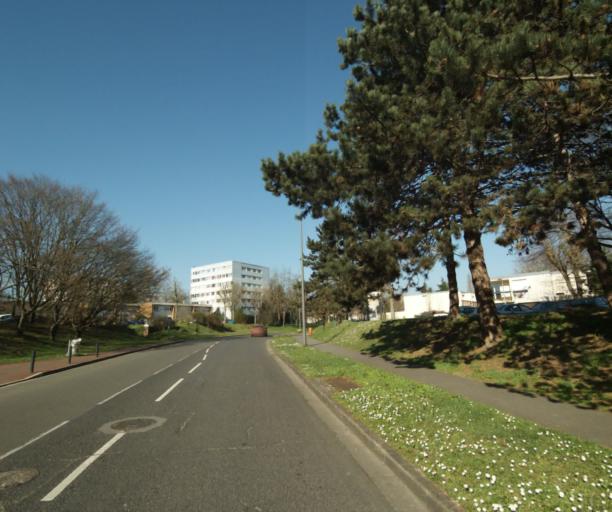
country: FR
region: Ile-de-France
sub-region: Departement du Val-d'Oise
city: Cergy
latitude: 49.0320
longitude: 2.0842
